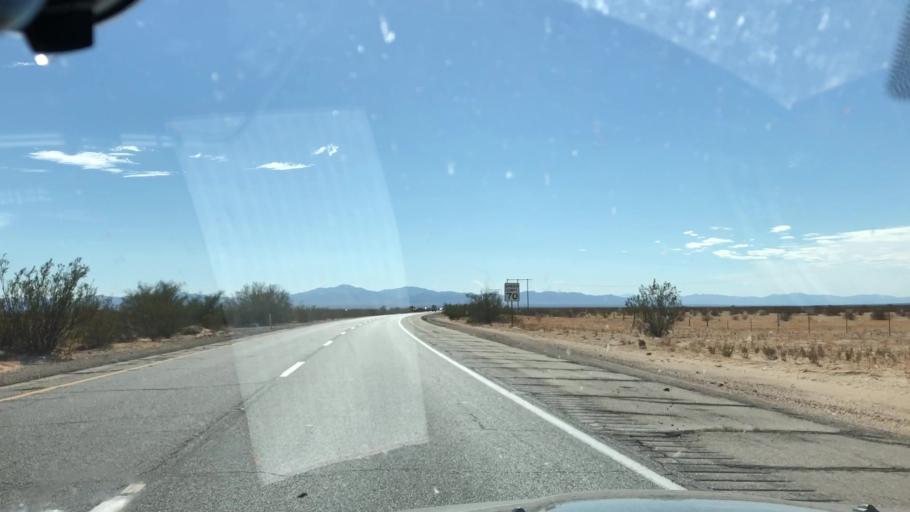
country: US
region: California
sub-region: Riverside County
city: Mesa Verde
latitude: 33.6063
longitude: -114.9243
